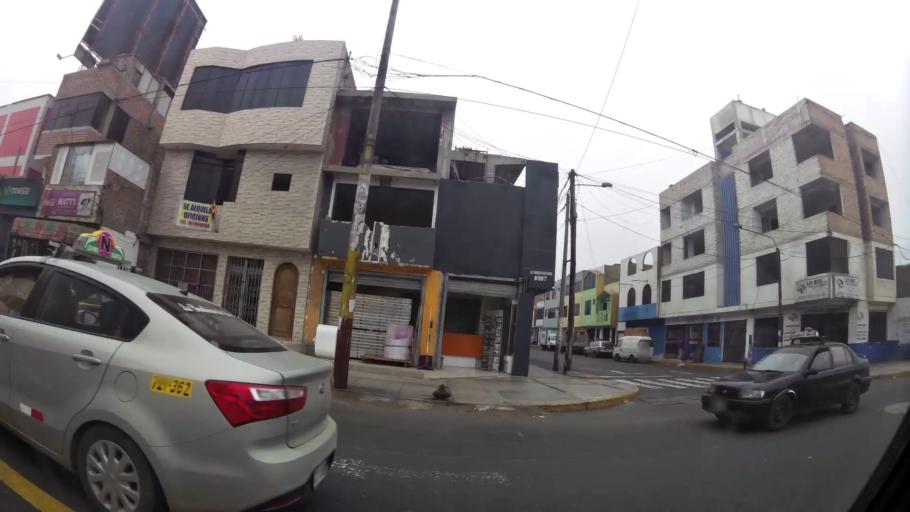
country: PE
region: Ancash
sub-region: Provincia de Santa
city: Chimbote
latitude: -9.0782
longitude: -78.5885
